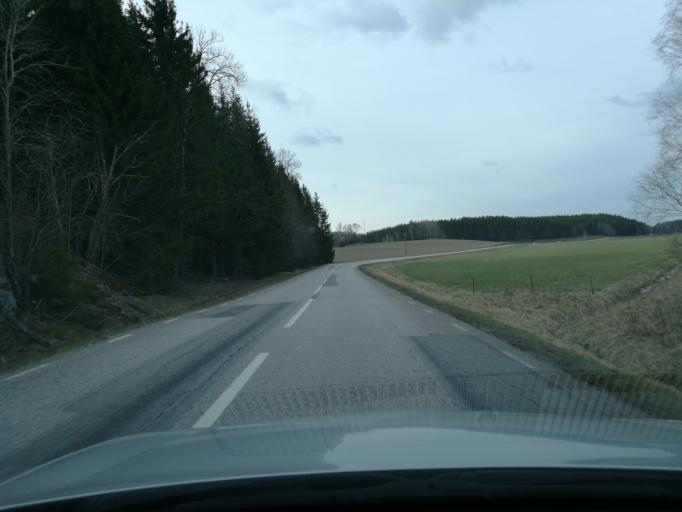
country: SE
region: Soedermanland
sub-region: Gnesta Kommun
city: Gnesta
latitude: 58.9407
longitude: 17.3468
